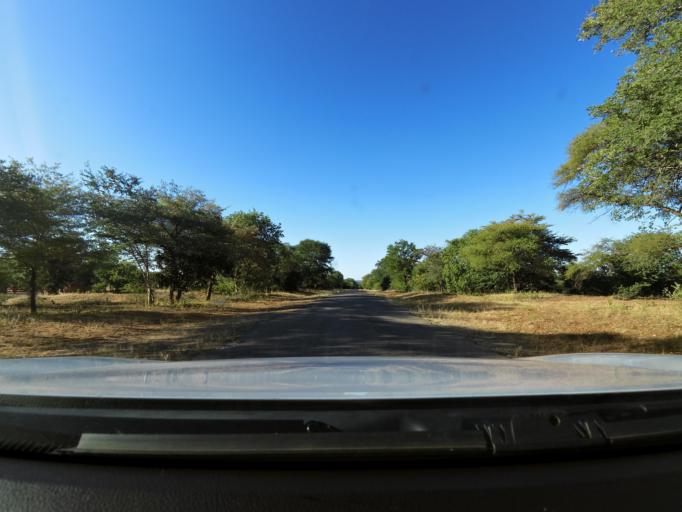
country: ZW
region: Matabeleland North
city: Kamativi Mine
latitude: -18.0693
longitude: 27.0954
